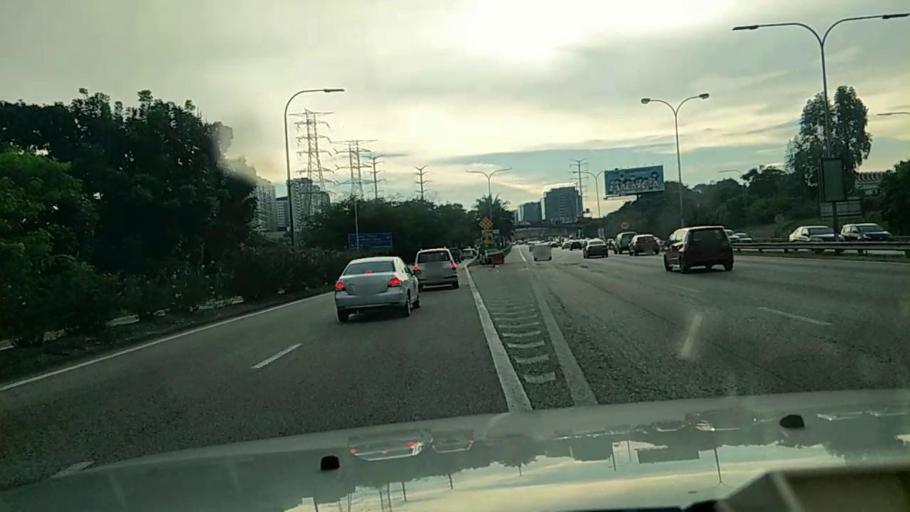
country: MY
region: Selangor
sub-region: Petaling
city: Petaling Jaya
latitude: 3.0837
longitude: 101.5979
